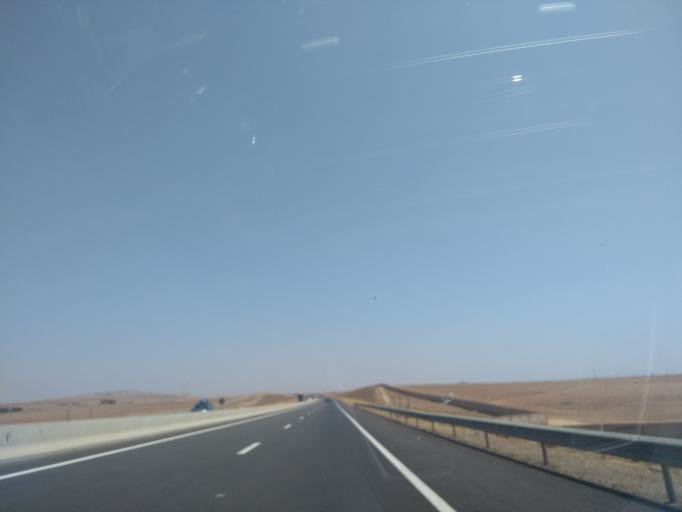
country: MA
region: Marrakech-Tensift-Al Haouz
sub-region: Kelaa-Des-Sraghna
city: Sidi Abdallah
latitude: 32.2906
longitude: -7.9630
